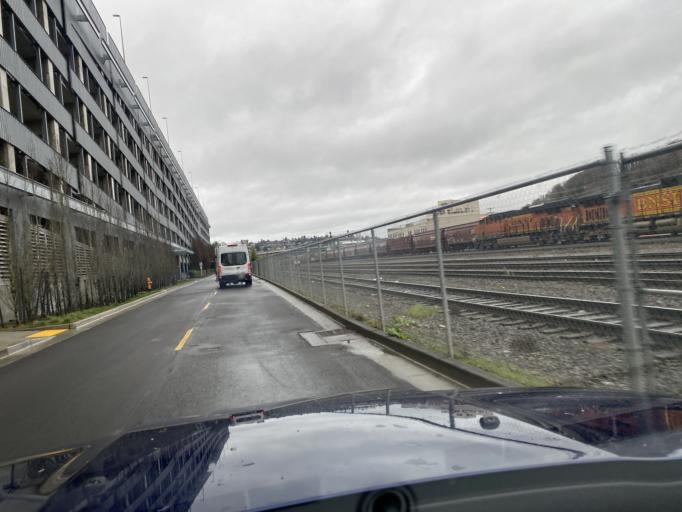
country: US
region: Washington
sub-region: King County
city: Seattle
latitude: 47.6288
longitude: -122.3734
